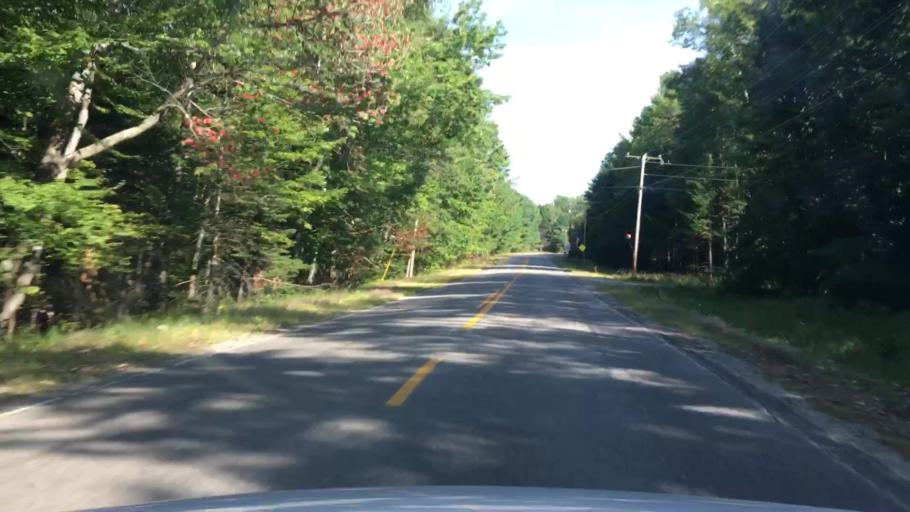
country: US
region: Maine
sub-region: Penobscot County
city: Enfield
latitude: 45.2377
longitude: -68.5487
